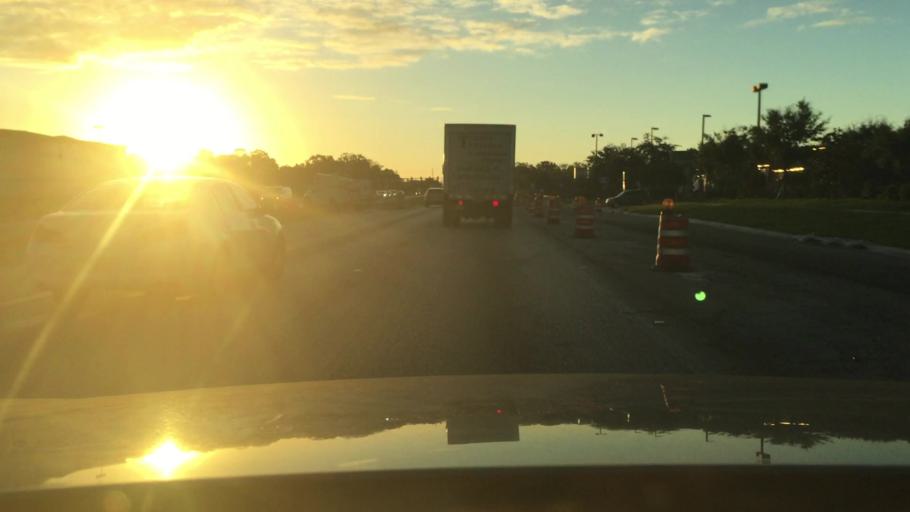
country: US
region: Florida
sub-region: Osceola County
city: Saint Cloud
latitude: 28.2542
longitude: -81.3180
